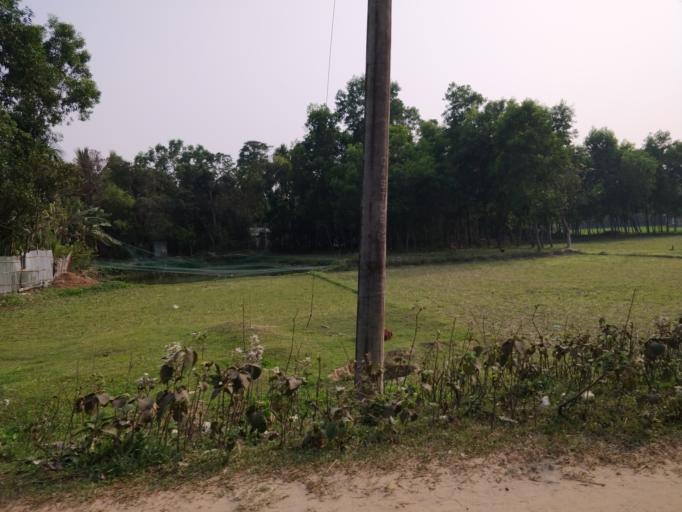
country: IN
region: Tripura
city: Khowai
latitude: 24.1297
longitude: 91.3694
